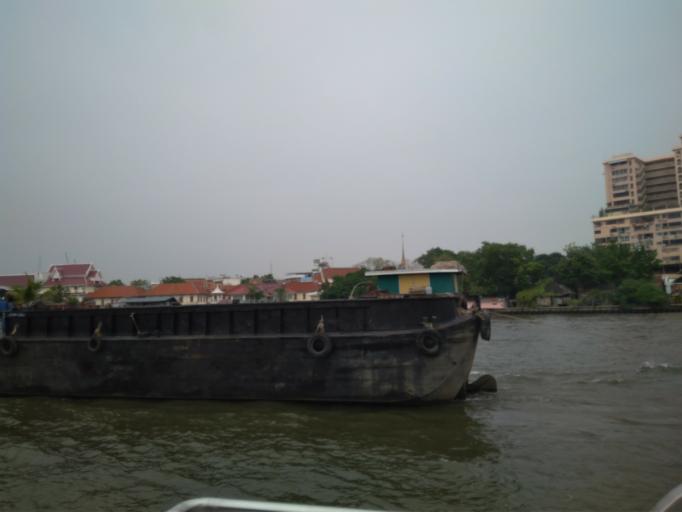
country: TH
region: Bangkok
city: Khlong San
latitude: 13.7338
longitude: 100.5103
